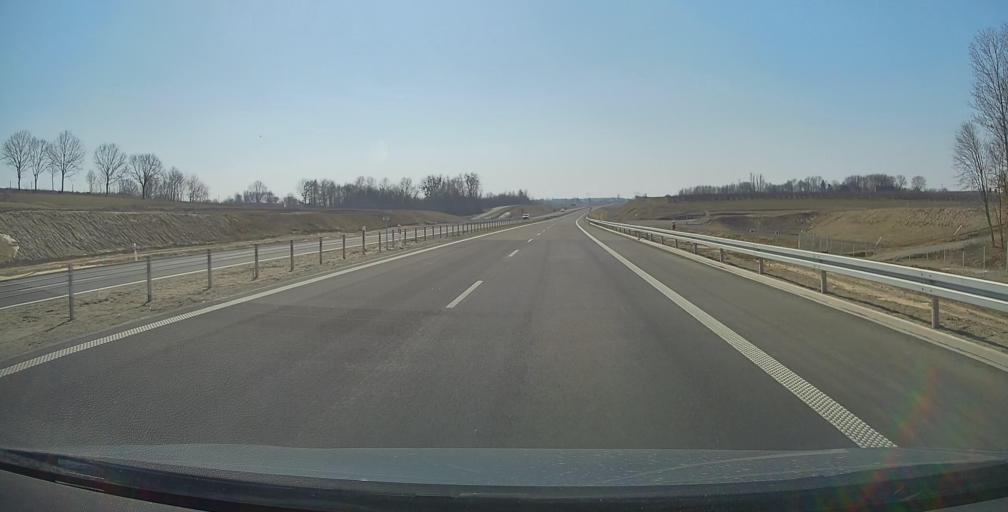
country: PL
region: Lublin Voivodeship
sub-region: Powiat krasnicki
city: Szastarka
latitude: 50.8164
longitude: 22.2999
